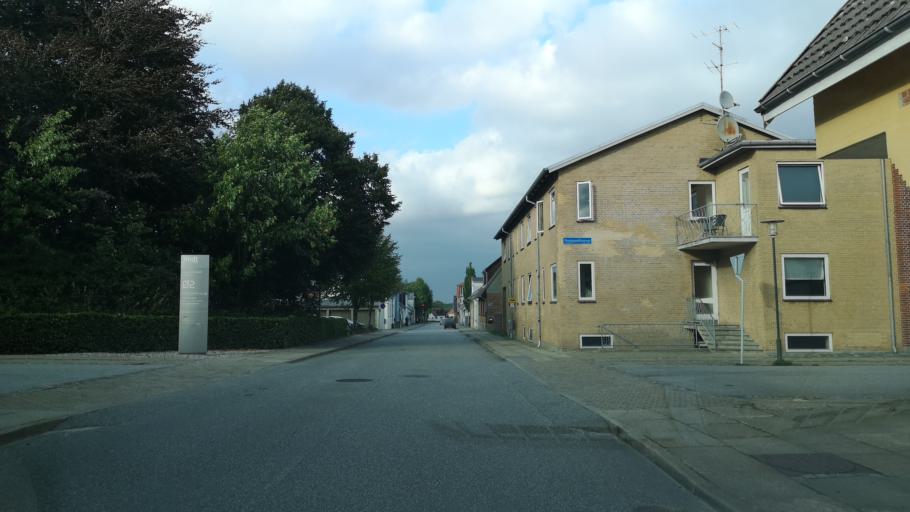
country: DK
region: Central Jutland
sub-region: Herning Kommune
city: Herning
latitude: 56.1391
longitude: 8.9737
